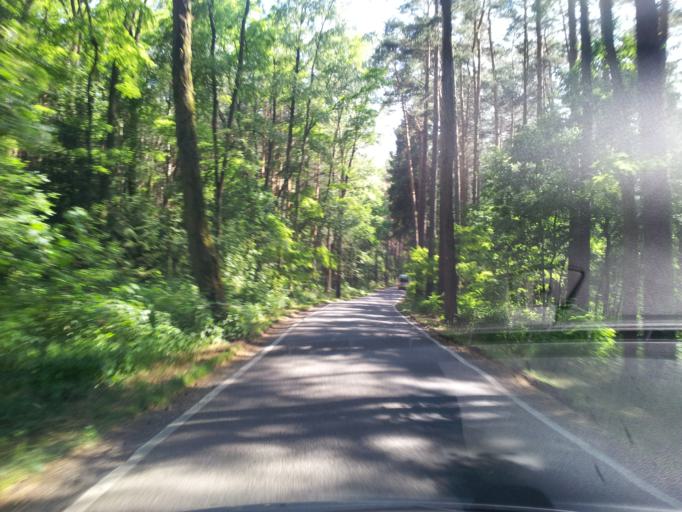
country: DE
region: Saxony
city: Hockendorf
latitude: 51.2095
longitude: 13.9028
